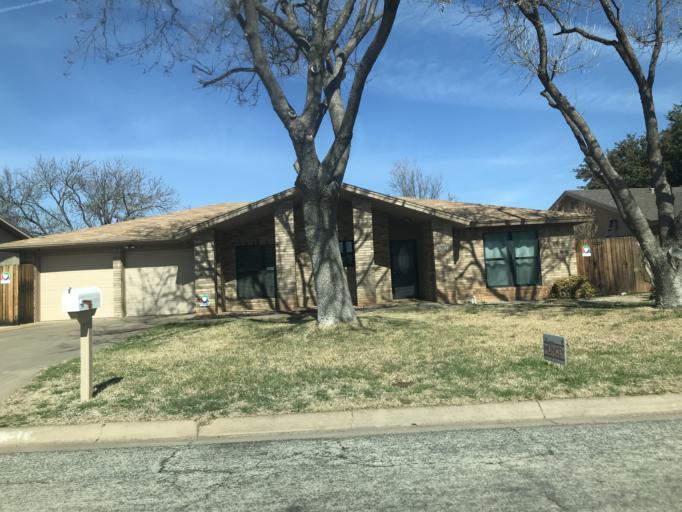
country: US
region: Texas
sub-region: Tom Green County
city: San Angelo
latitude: 31.4340
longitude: -100.4856
